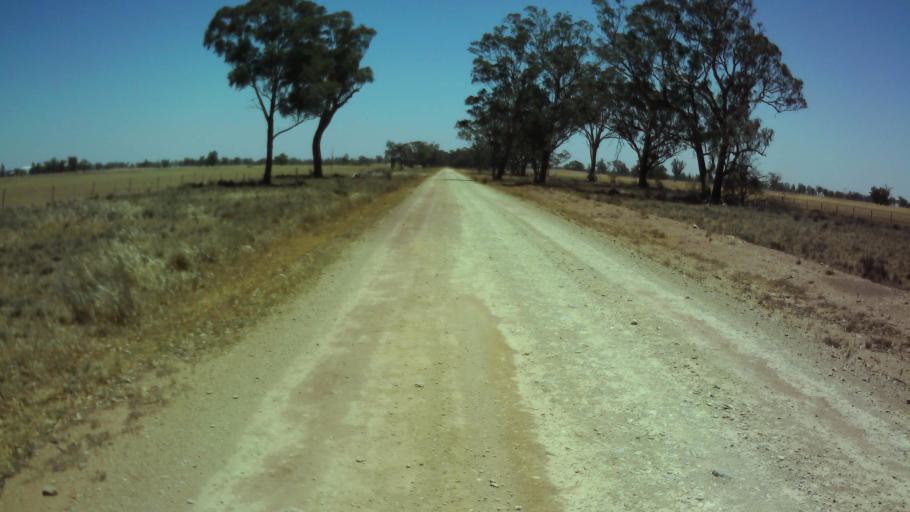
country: AU
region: New South Wales
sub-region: Weddin
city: Grenfell
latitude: -34.0294
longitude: 147.8708
